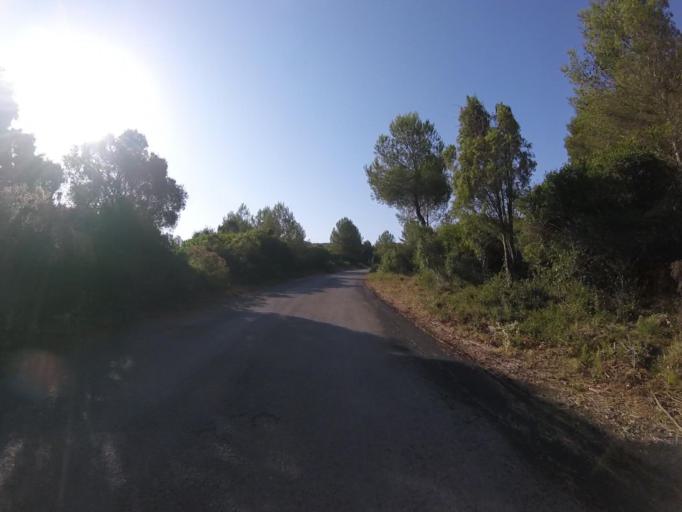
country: ES
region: Valencia
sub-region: Provincia de Castello
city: Cabanes
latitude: 40.1082
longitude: 0.0641
